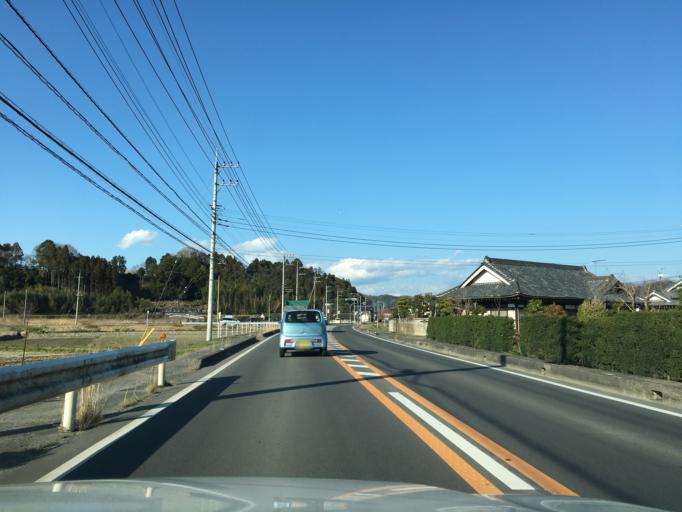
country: JP
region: Ibaraki
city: Omiya
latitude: 36.5848
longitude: 140.4082
